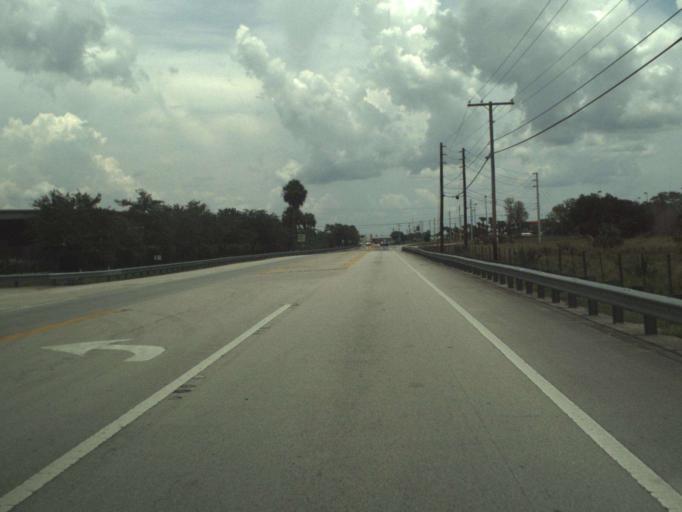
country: US
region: Florida
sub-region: Saint Lucie County
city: Lakewood Park
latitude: 27.4418
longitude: -80.3990
